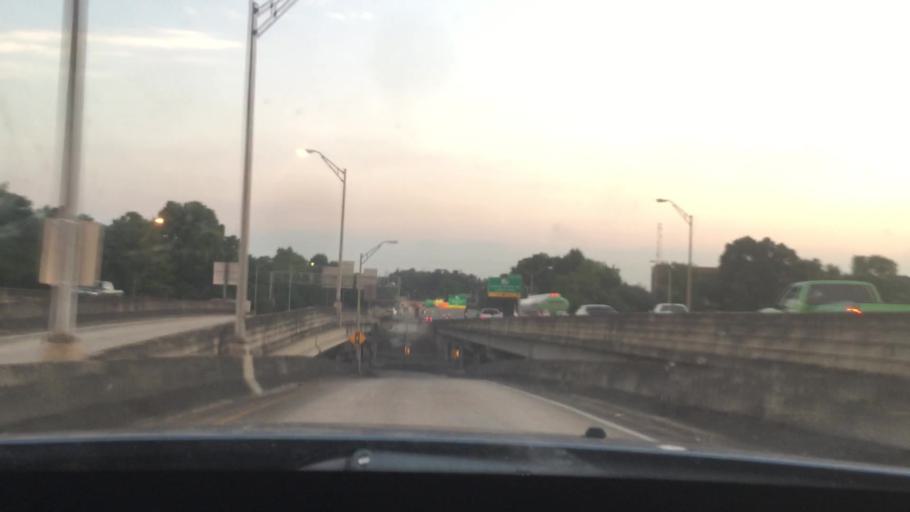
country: US
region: Louisiana
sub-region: East Baton Rouge Parish
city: Baton Rouge
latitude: 30.4516
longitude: -91.1805
